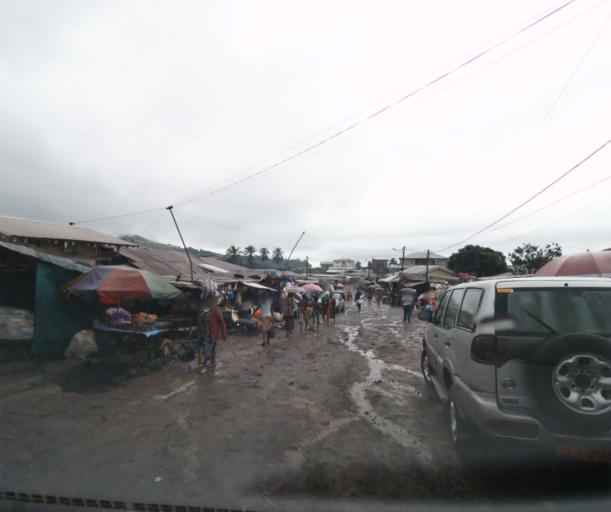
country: CM
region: South-West Province
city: Limbe
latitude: 4.0104
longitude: 9.2142
